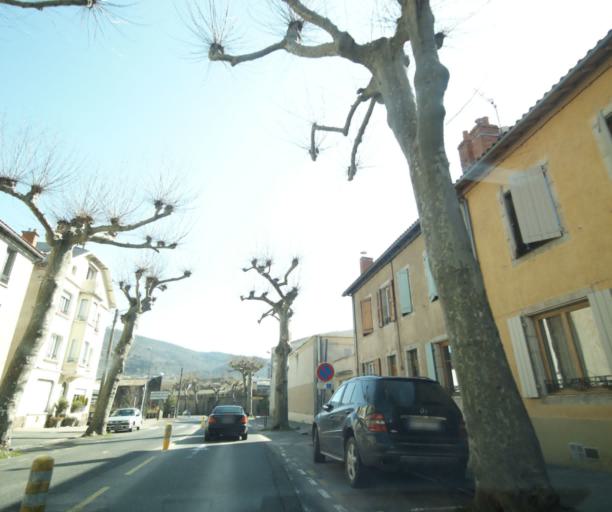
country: FR
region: Midi-Pyrenees
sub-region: Departement de l'Aveyron
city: Saint-Affrique
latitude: 43.9558
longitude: 2.8835
